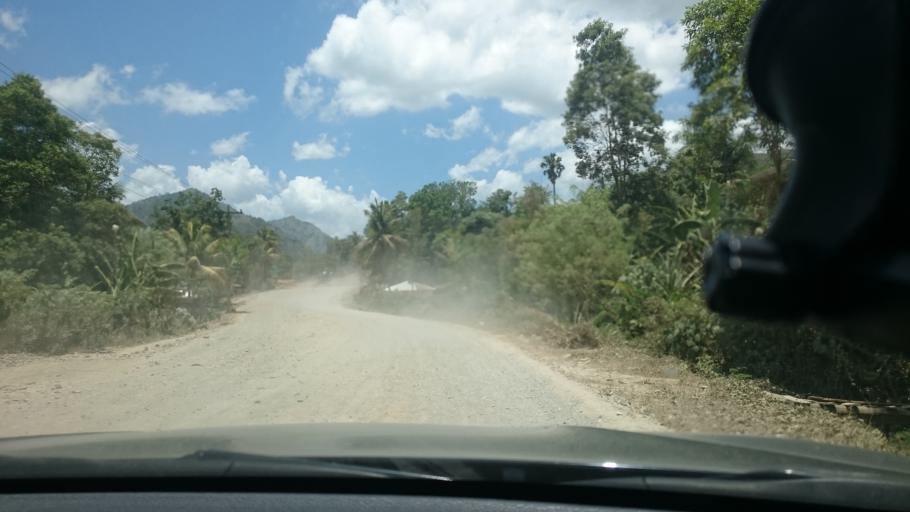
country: HT
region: Nord
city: Milot
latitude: 19.6239
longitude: -72.1977
